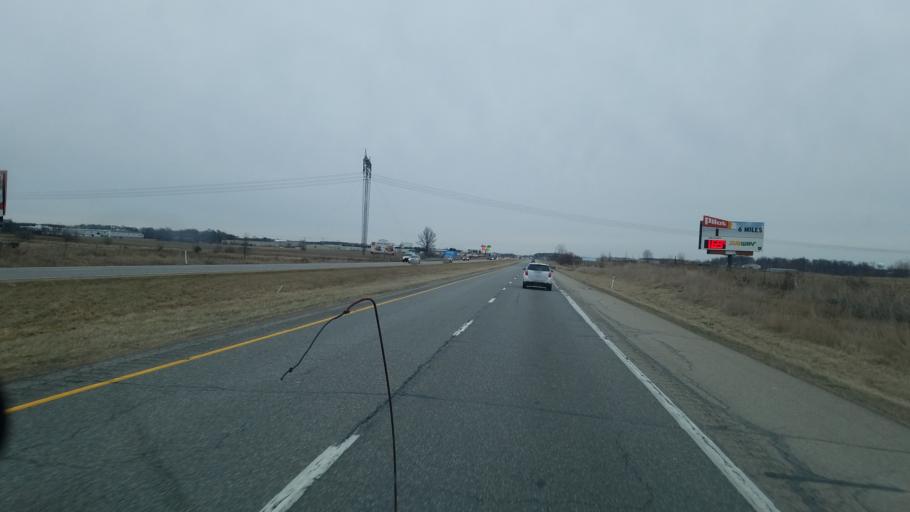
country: US
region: Indiana
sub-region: Marshall County
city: Plymouth
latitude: 41.3612
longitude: -86.3624
